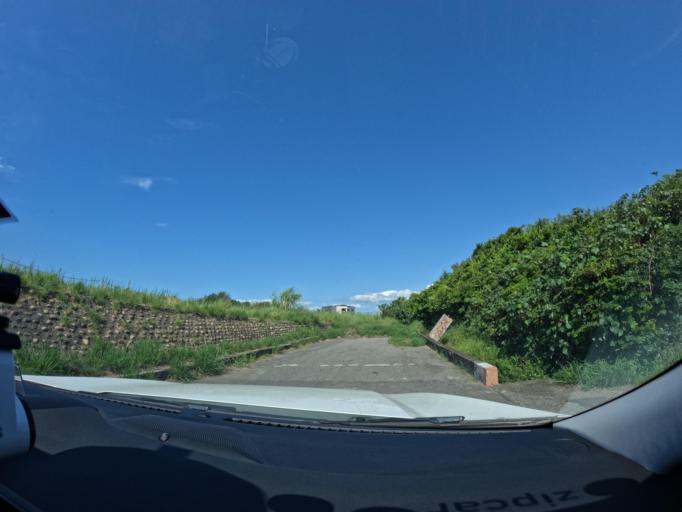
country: TW
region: Taiwan
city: Taoyuan City
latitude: 25.0954
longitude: 121.1942
